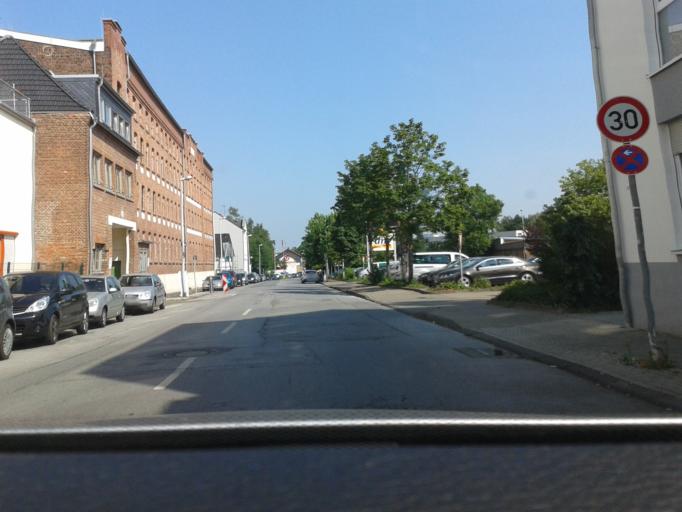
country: DE
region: North Rhine-Westphalia
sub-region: Regierungsbezirk Dusseldorf
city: Muelheim (Ruhr)
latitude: 51.4297
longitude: 6.8440
